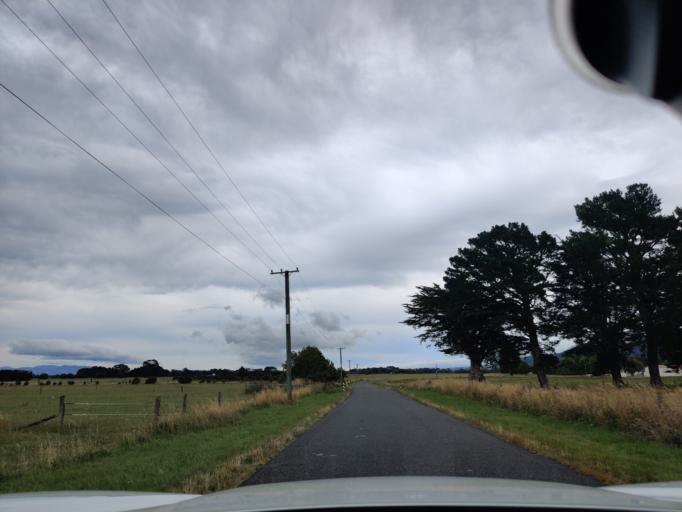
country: NZ
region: Wellington
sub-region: Masterton District
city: Masterton
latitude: -41.0277
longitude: 175.4527
